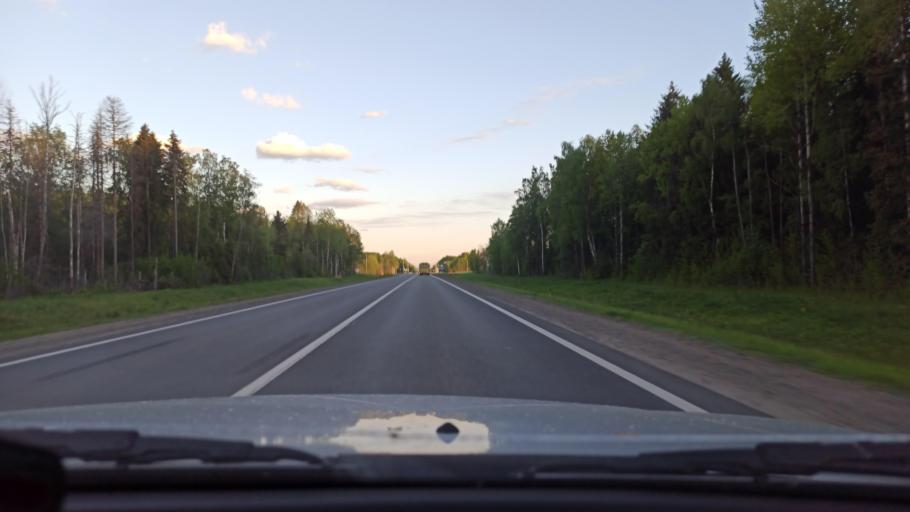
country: RU
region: Vologda
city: Molochnoye
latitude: 59.3292
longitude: 39.6820
